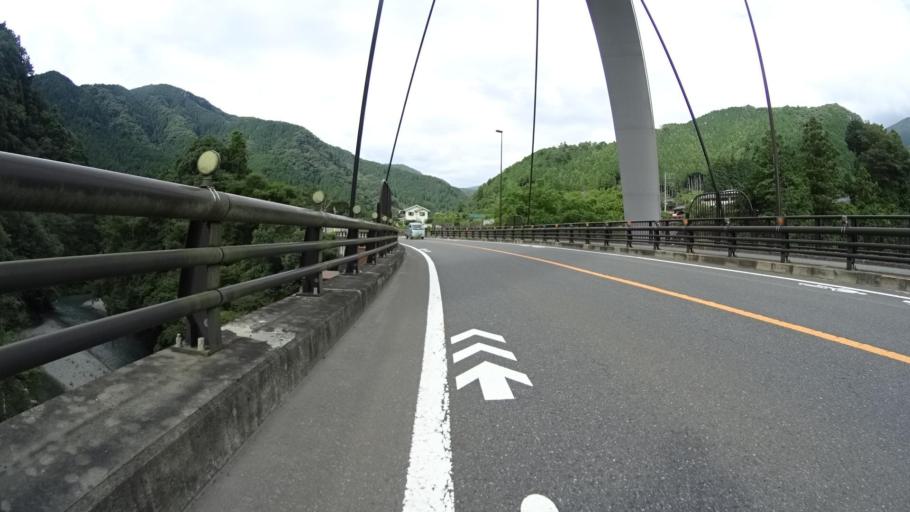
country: JP
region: Tokyo
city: Itsukaichi
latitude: 35.7264
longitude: 139.1828
